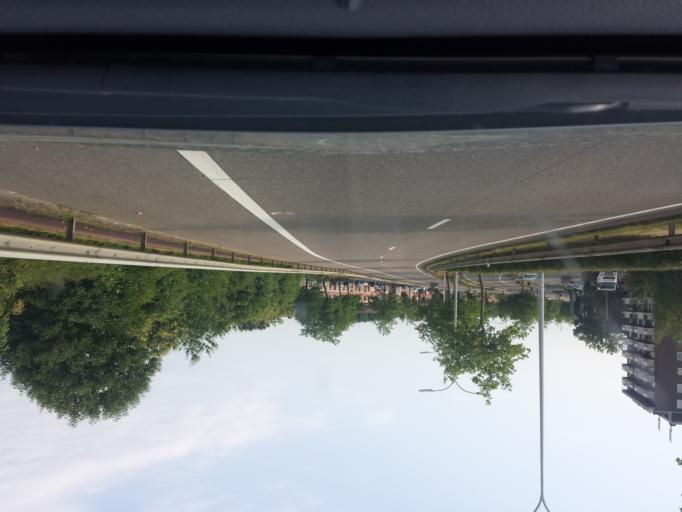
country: BE
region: Flanders
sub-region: Provincie Limburg
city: Hasselt
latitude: 50.9316
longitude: 5.3136
